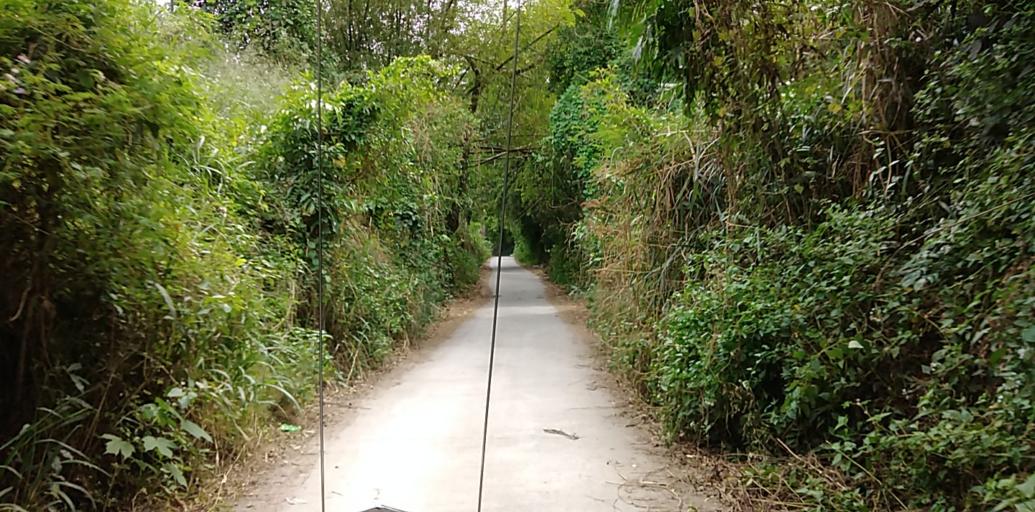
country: PH
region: Central Luzon
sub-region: Province of Pampanga
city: Porac
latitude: 15.0571
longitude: 120.5335
